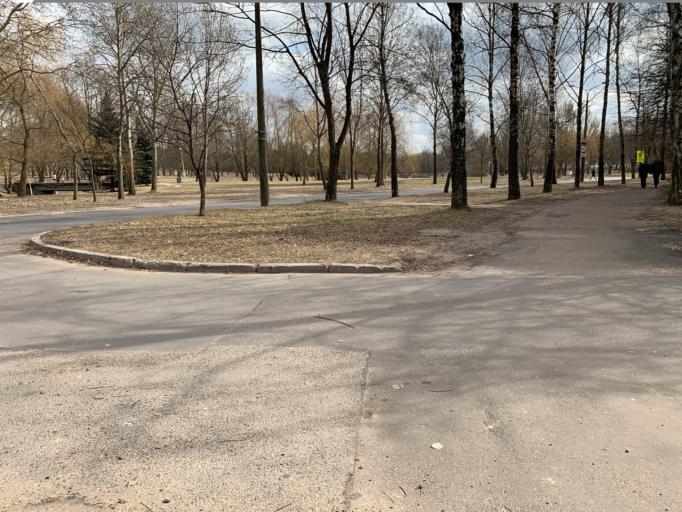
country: BY
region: Minsk
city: Borovlyany
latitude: 53.9513
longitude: 27.6289
